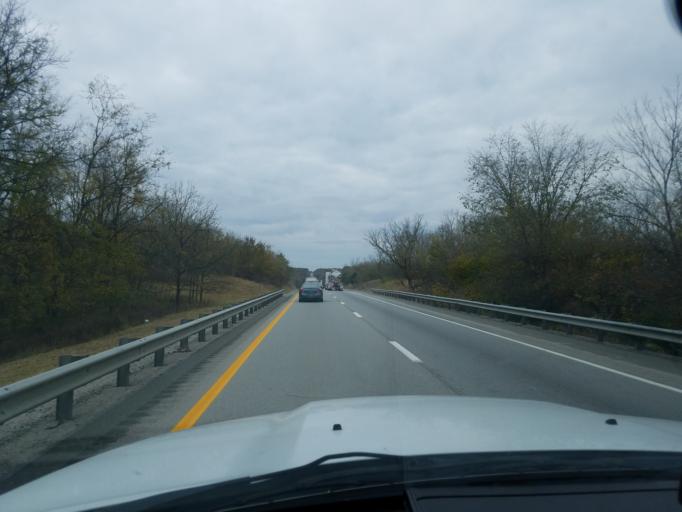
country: US
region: Kentucky
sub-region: Oldham County
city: La Grange
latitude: 38.4290
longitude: -85.3225
